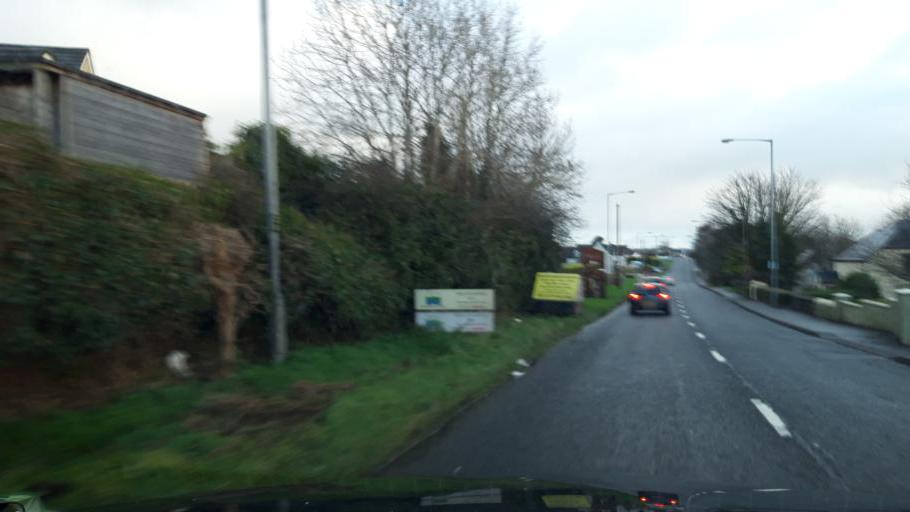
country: GB
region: Northern Ireland
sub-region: Moyle District
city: Ballycastle
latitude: 55.1948
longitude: -6.2664
